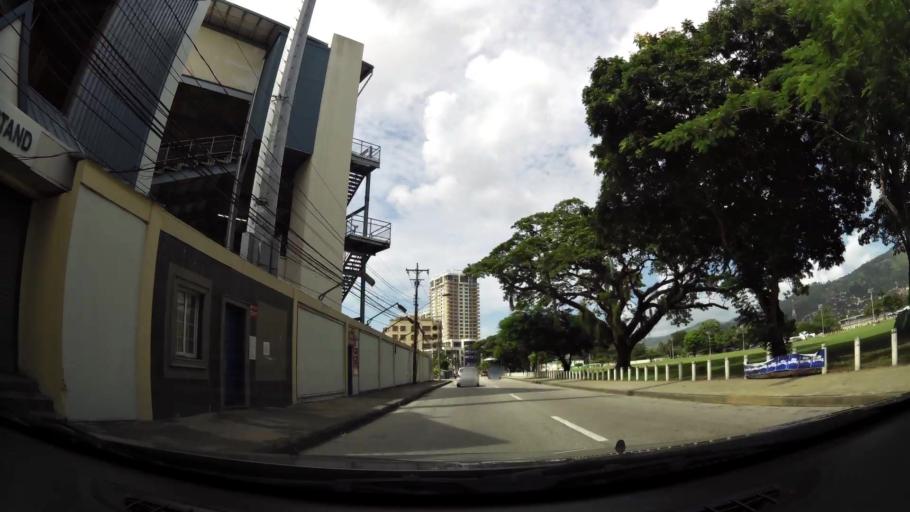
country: TT
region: City of Port of Spain
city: Port-of-Spain
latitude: 10.6682
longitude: -61.5239
